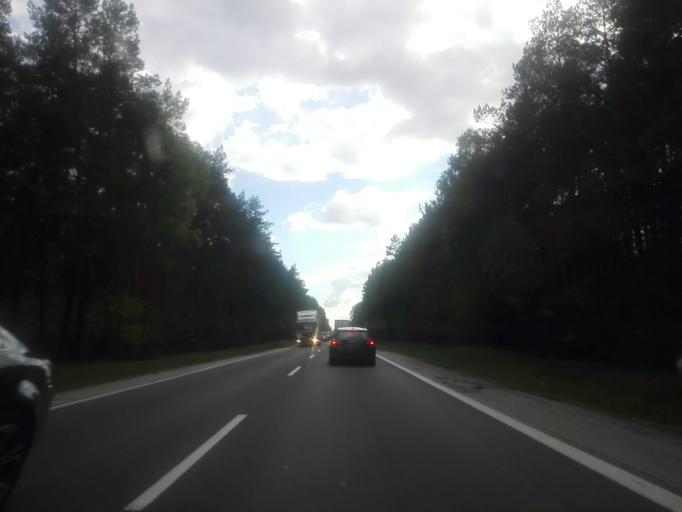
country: PL
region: Masovian Voivodeship
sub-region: Powiat ostrowski
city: Brok
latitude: 52.7320
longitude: 21.7374
